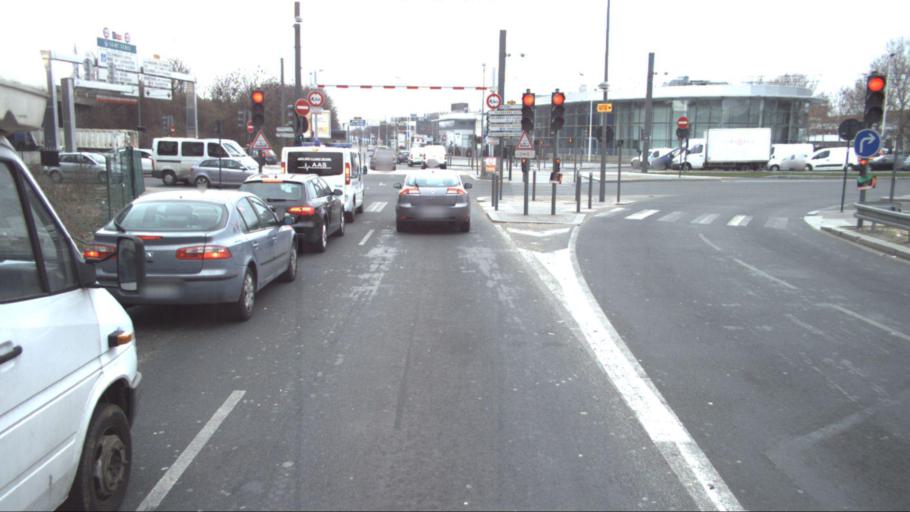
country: FR
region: Ile-de-France
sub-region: Departement du Val-d'Oise
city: Bezons
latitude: 48.9193
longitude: 2.2233
